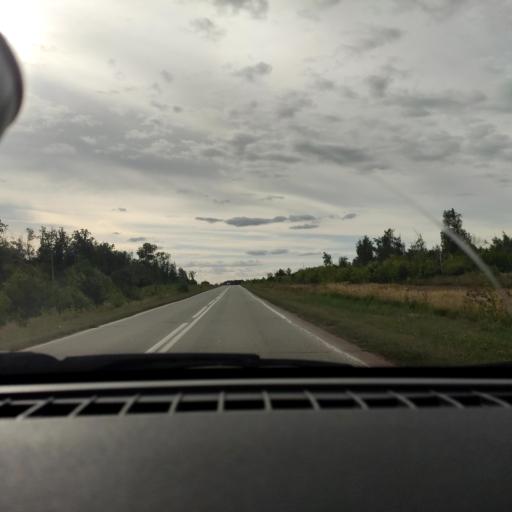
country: RU
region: Samara
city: Georgiyevka
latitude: 53.4256
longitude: 50.8174
